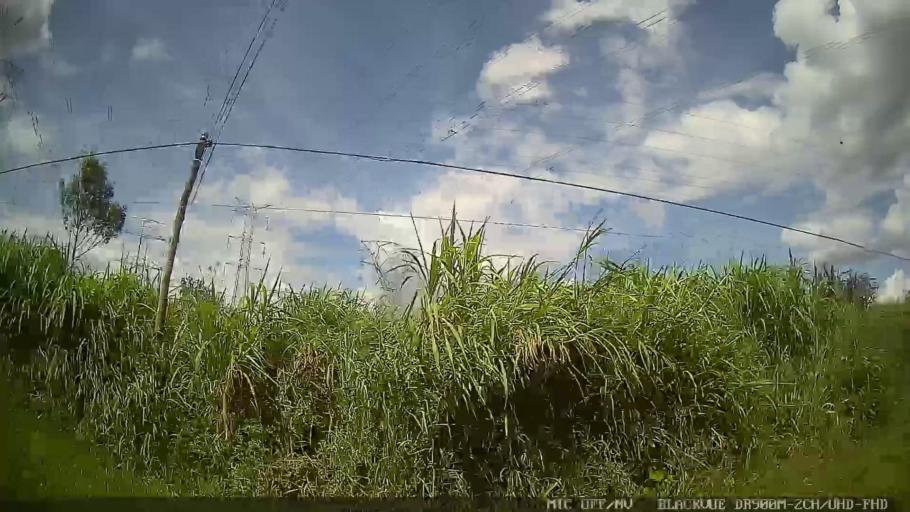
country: BR
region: Sao Paulo
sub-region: Suzano
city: Suzano
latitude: -23.6659
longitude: -46.2333
